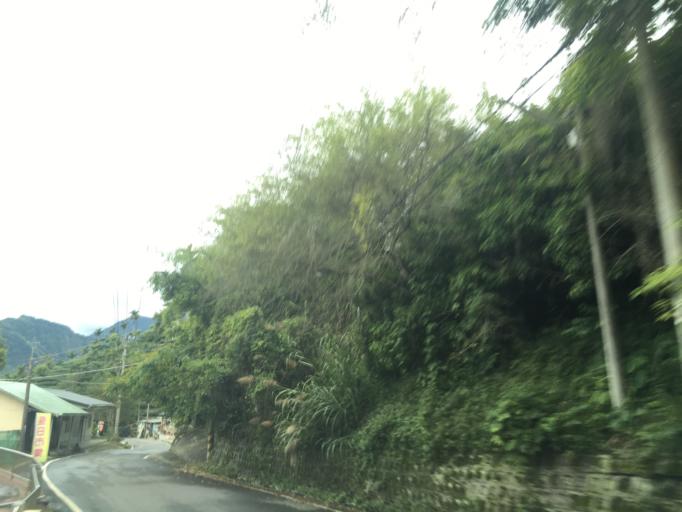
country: TW
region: Taiwan
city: Lugu
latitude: 23.5417
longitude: 120.7150
